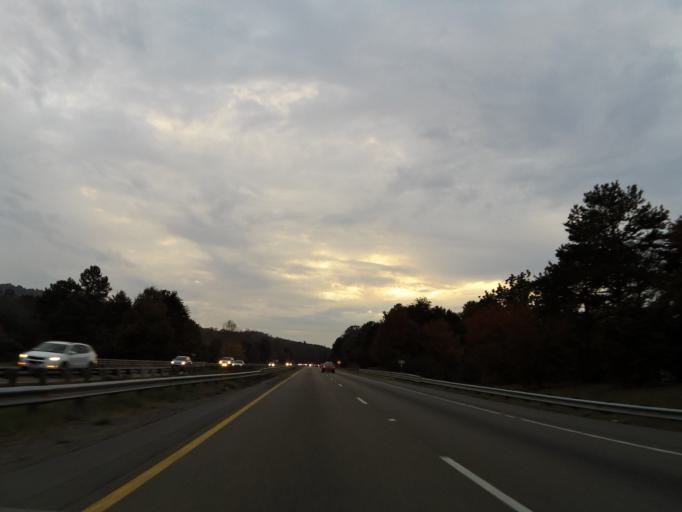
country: US
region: North Carolina
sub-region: Burke County
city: Valdese
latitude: 35.7301
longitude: -81.5449
